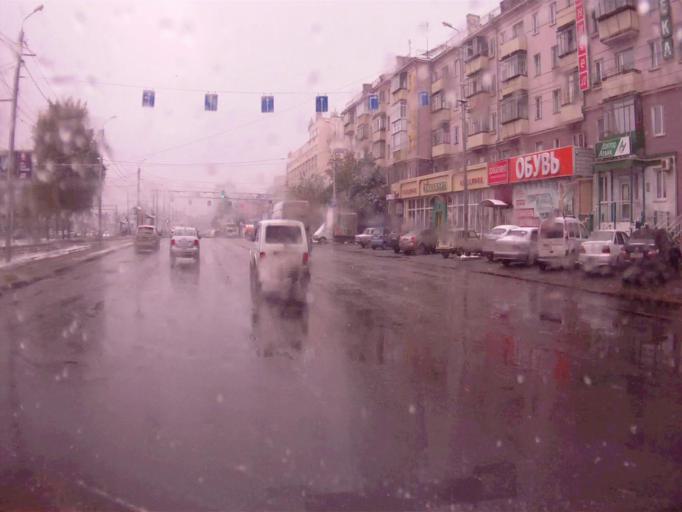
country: RU
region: Chelyabinsk
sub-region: Gorod Chelyabinsk
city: Chelyabinsk
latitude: 55.1430
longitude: 61.4136
